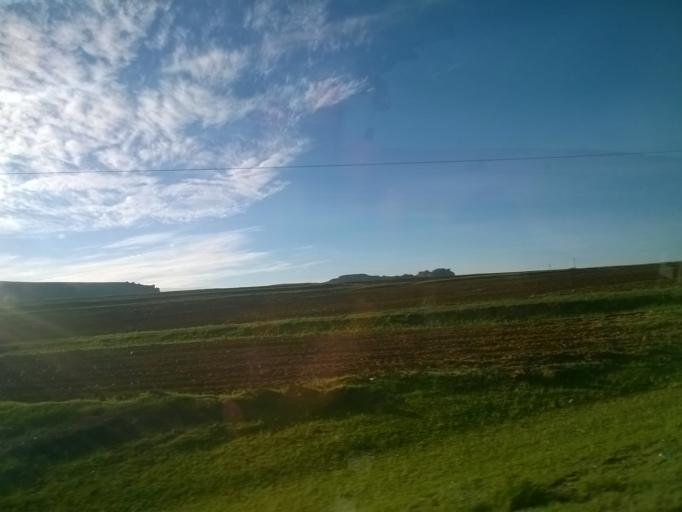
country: LS
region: Berea
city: Teyateyaneng
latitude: -29.1782
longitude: 27.6267
